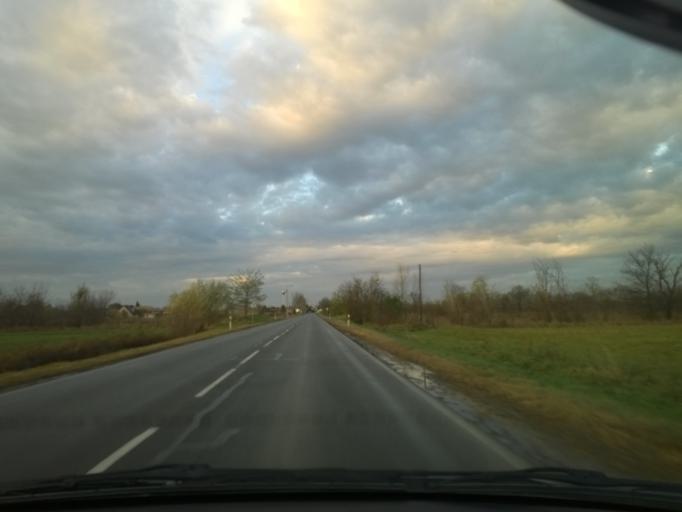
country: HU
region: Bacs-Kiskun
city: Solt
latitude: 46.7886
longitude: 19.0035
